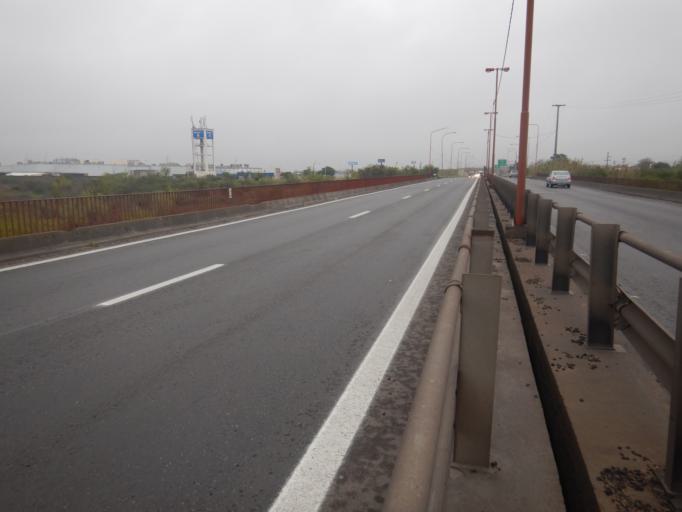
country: AR
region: Santa Fe
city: Santa Fe de la Vera Cruz
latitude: -31.6398
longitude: -60.6535
